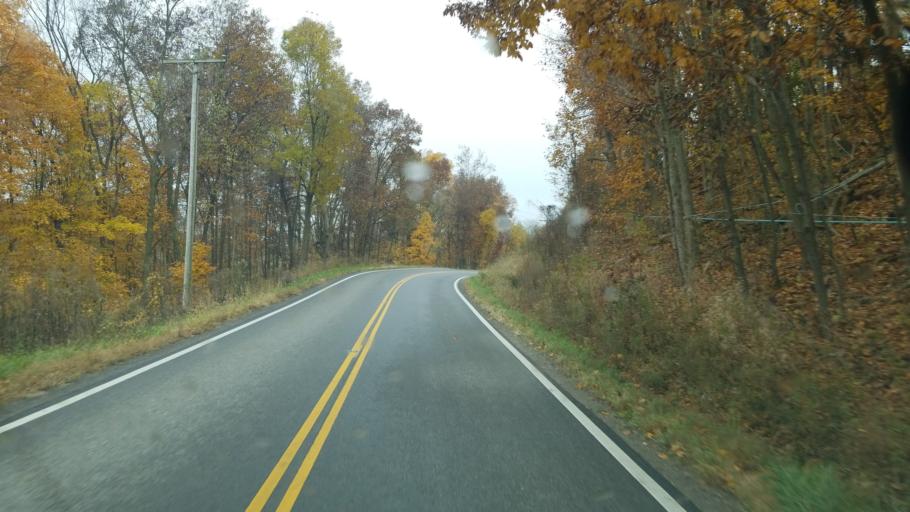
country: US
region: Ohio
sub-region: Coshocton County
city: Coshocton
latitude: 40.3847
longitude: -81.8170
